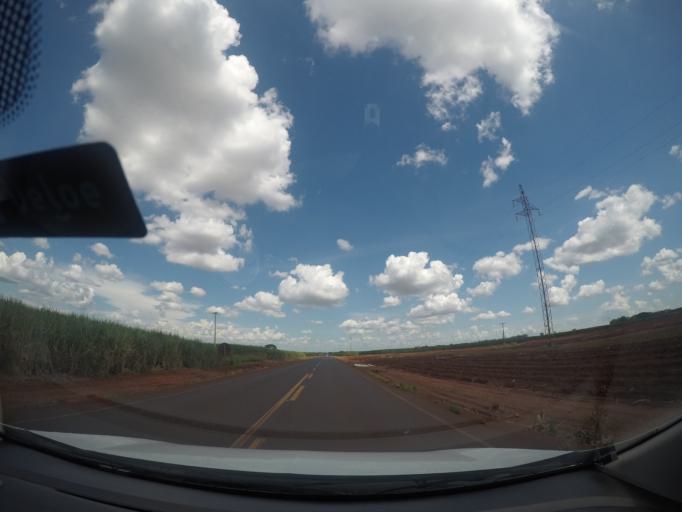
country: BR
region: Minas Gerais
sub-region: Frutal
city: Frutal
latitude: -19.8496
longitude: -48.7368
